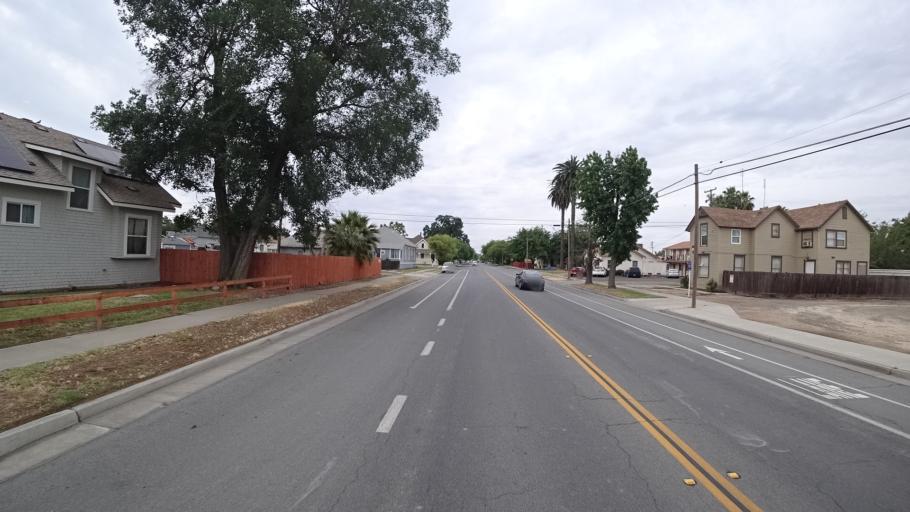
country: US
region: California
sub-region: Kings County
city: Hanford
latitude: 36.3339
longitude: -119.6493
